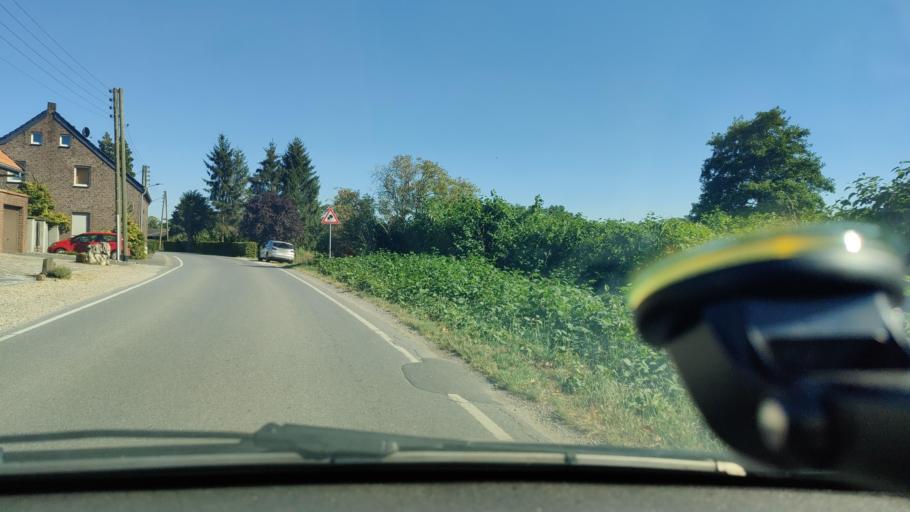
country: DE
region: North Rhine-Westphalia
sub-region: Regierungsbezirk Dusseldorf
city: Wachtendonk
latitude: 51.4388
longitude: 6.3931
